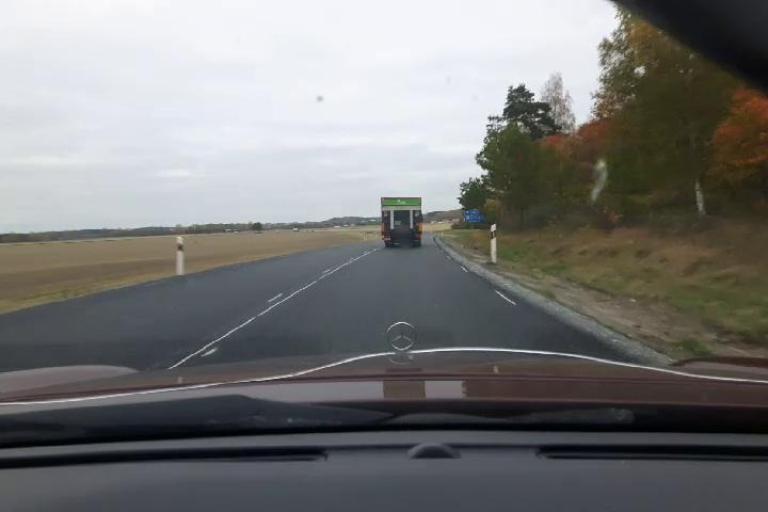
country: SE
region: Uppsala
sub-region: Enkopings Kommun
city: Enkoping
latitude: 59.6158
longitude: 17.0367
